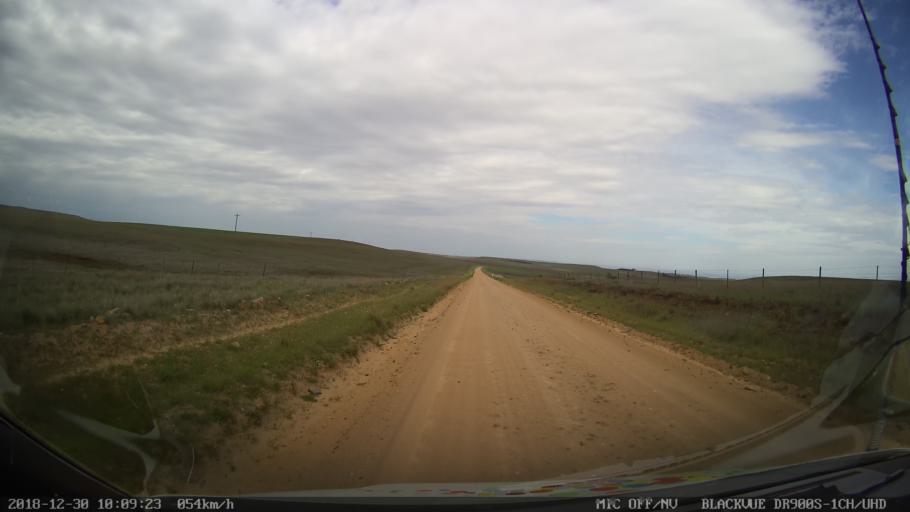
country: AU
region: New South Wales
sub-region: Cooma-Monaro
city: Cooma
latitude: -36.5481
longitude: 149.1060
